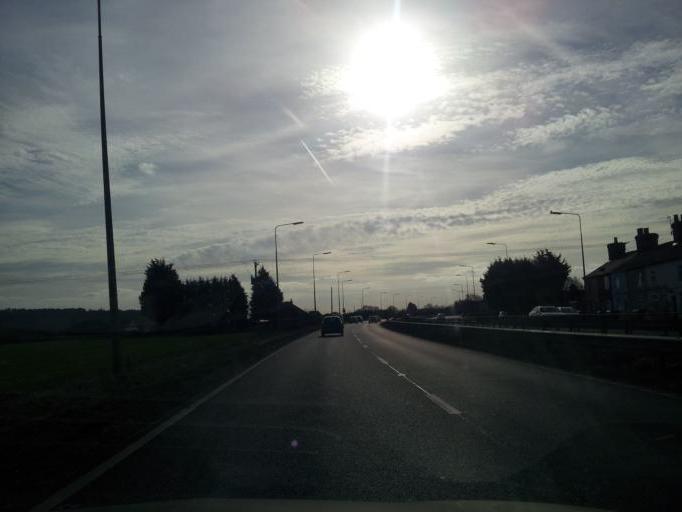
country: GB
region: England
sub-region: Central Bedfordshire
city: Sandy
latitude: 52.1201
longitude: -0.2906
